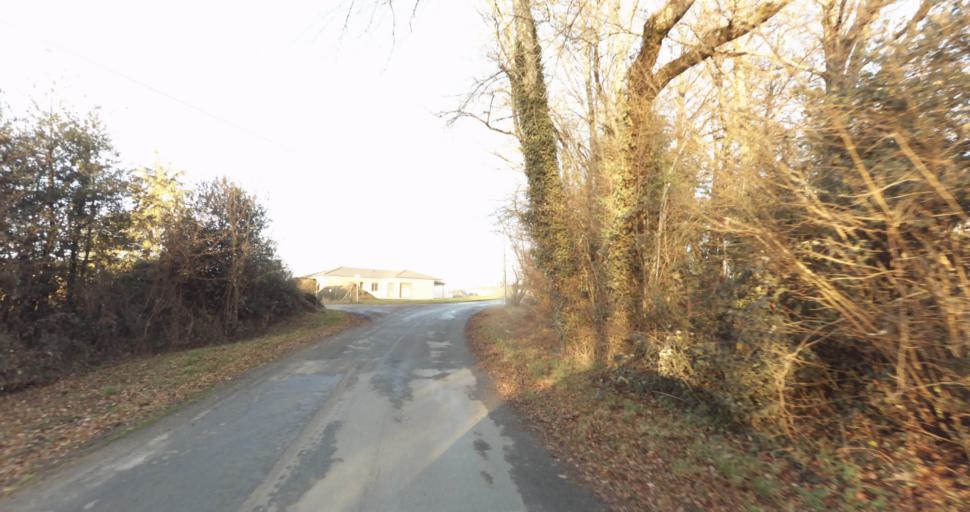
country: FR
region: Limousin
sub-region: Departement de la Haute-Vienne
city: Aixe-sur-Vienne
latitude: 45.8133
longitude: 1.1330
